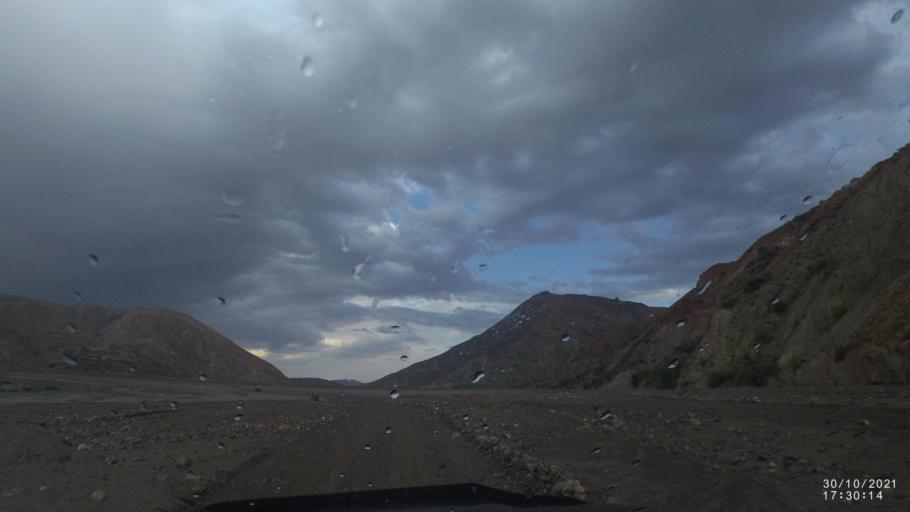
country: BO
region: Cochabamba
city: Sipe Sipe
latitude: -17.5238
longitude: -66.5985
